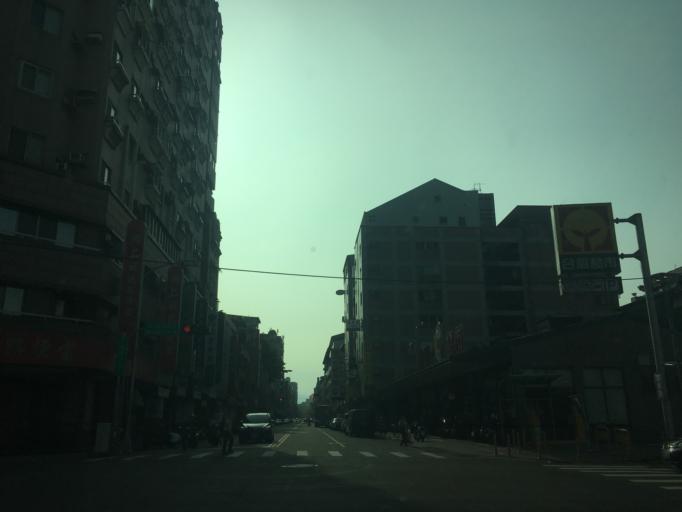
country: TW
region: Taiwan
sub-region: Taichung City
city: Taichung
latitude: 24.1698
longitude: 120.6792
